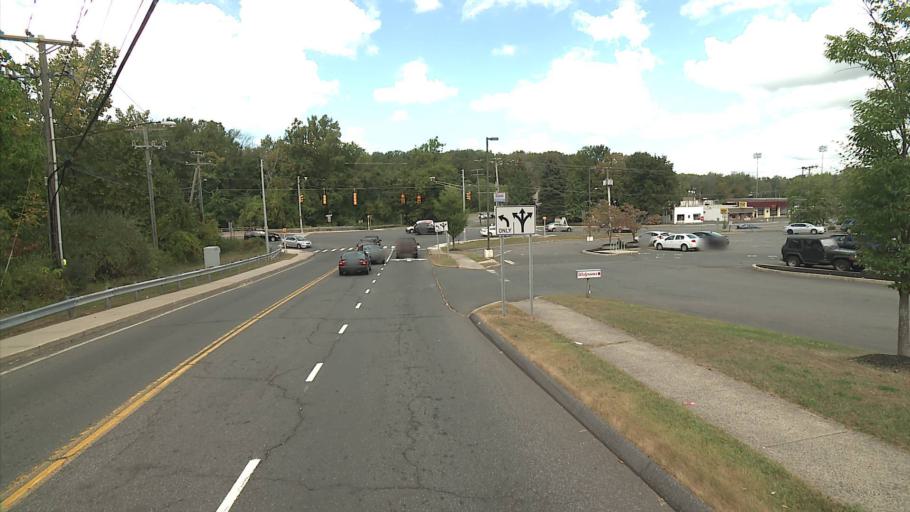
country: US
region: Connecticut
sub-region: Middlesex County
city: Middletown
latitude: 41.5543
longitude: -72.6733
